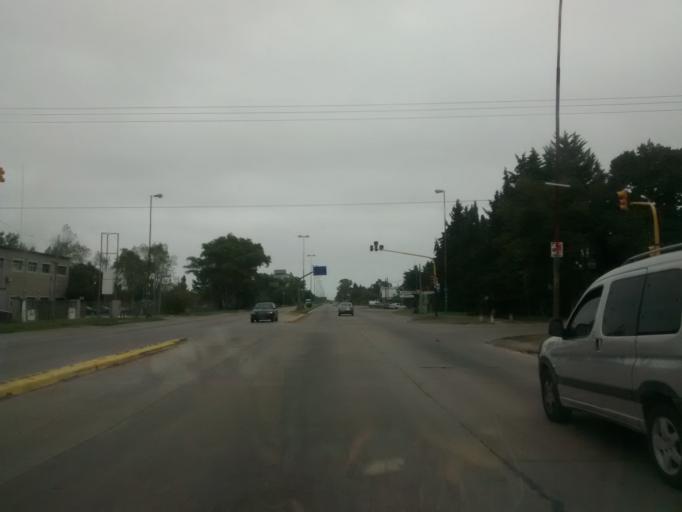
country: AR
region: Buenos Aires
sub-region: Partido de La Plata
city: La Plata
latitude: -35.0056
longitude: -58.0597
